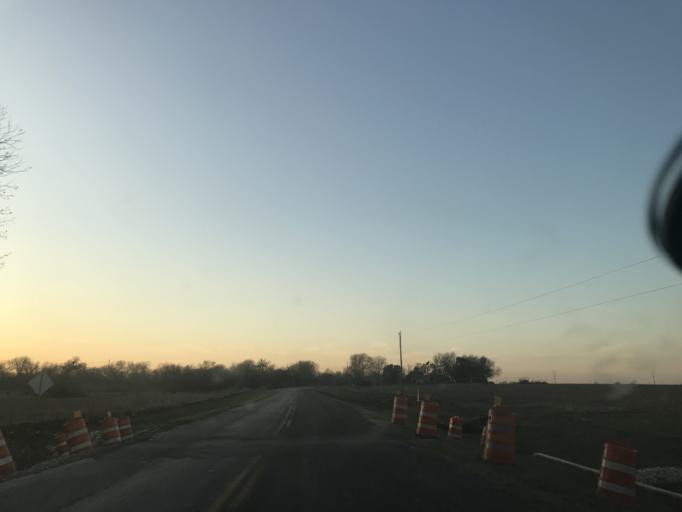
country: US
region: Texas
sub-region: Williamson County
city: Hutto
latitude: 30.5019
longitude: -97.5150
